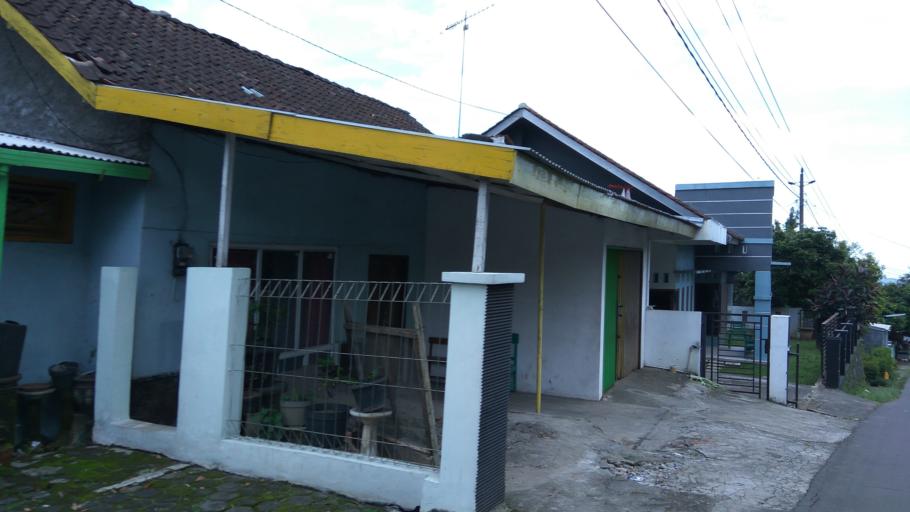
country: ID
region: Central Java
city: Ambarawa
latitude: -7.2353
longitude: 110.3814
